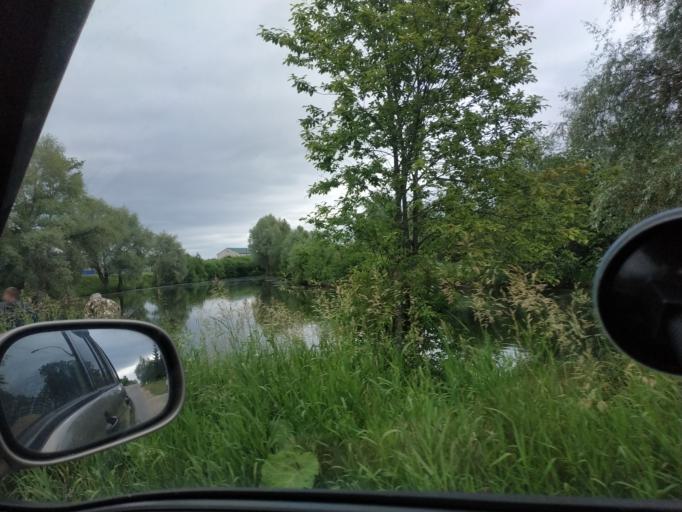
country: RU
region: Moskovskaya
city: Krasnoarmeysk
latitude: 56.0878
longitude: 38.2256
